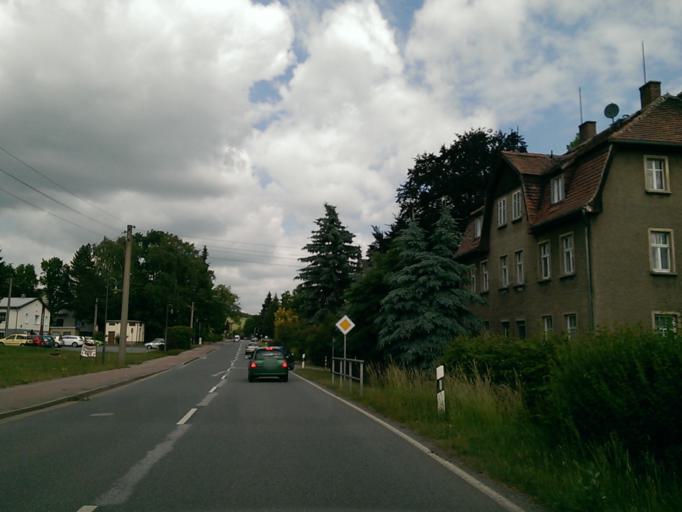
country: DE
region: Saxony
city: Eibau
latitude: 50.9733
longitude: 14.7004
